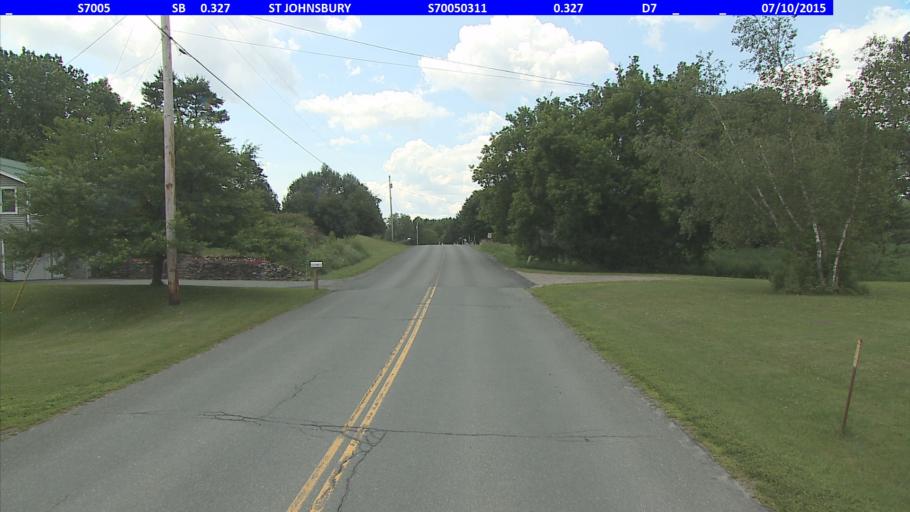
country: US
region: Vermont
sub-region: Caledonia County
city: St Johnsbury
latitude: 44.4390
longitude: -72.0081
